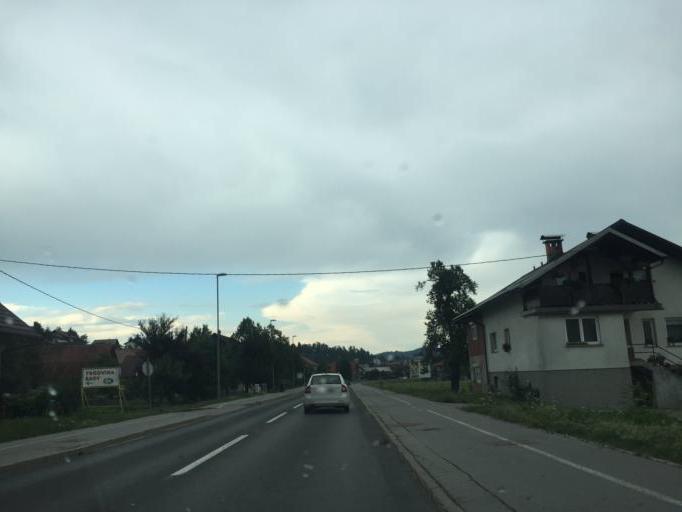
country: SI
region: Logatec
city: Logatec
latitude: 45.9133
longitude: 14.2081
